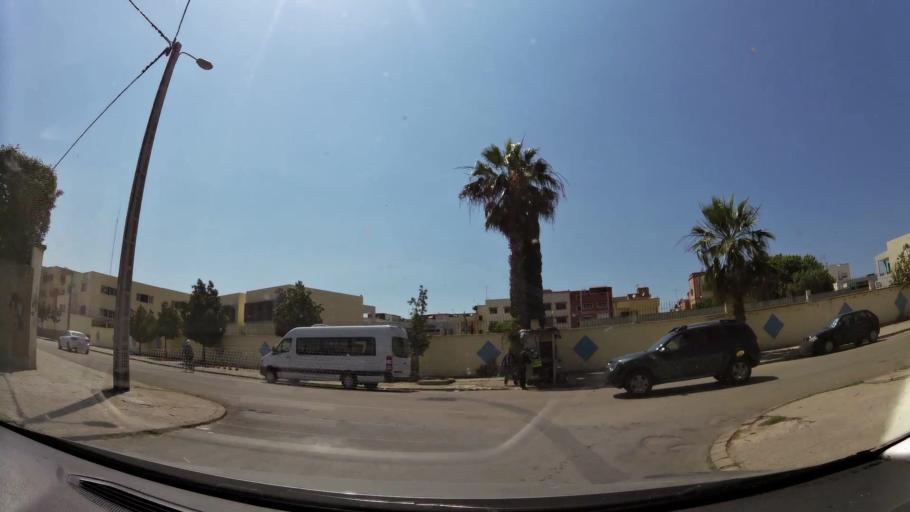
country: MA
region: Rabat-Sale-Zemmour-Zaer
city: Sale
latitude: 34.0450
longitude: -6.7868
